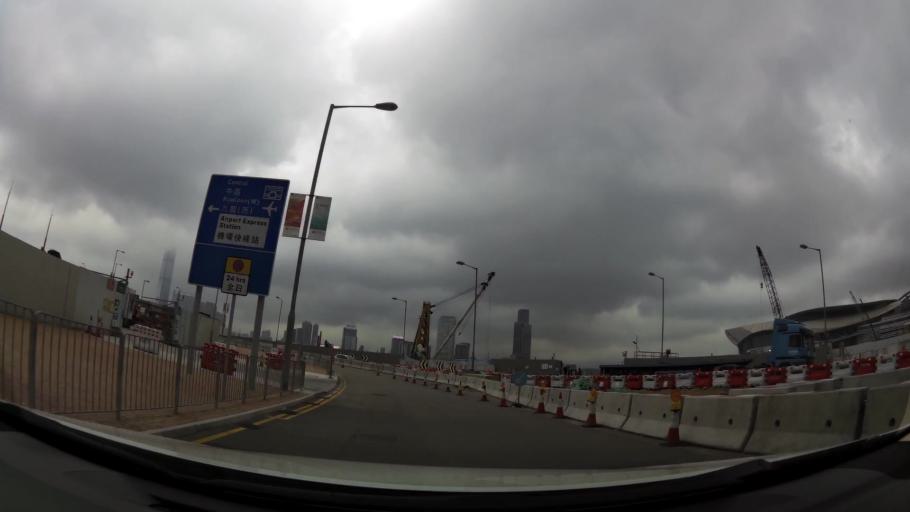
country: HK
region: Wanchai
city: Wan Chai
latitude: 22.2815
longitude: 114.1683
